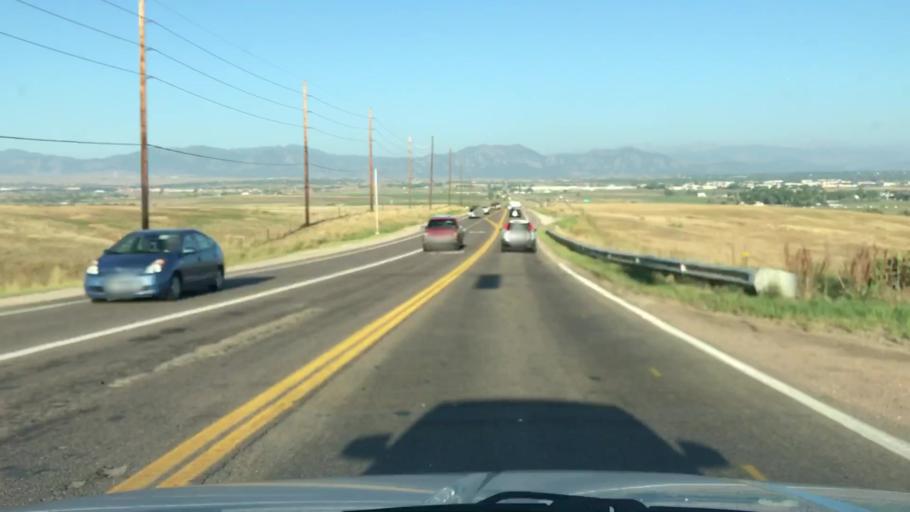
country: US
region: Colorado
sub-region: Broomfield County
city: Broomfield
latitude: 39.9563
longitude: -105.0730
